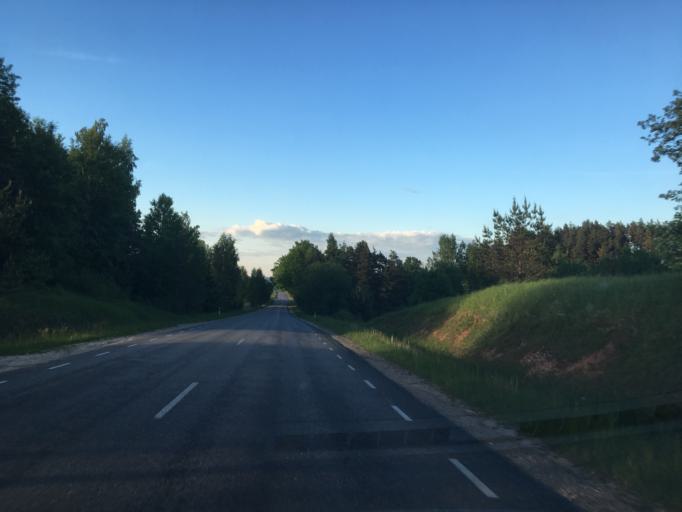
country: EE
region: Tartu
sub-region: Noo vald
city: Noo
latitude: 58.2217
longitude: 26.6301
